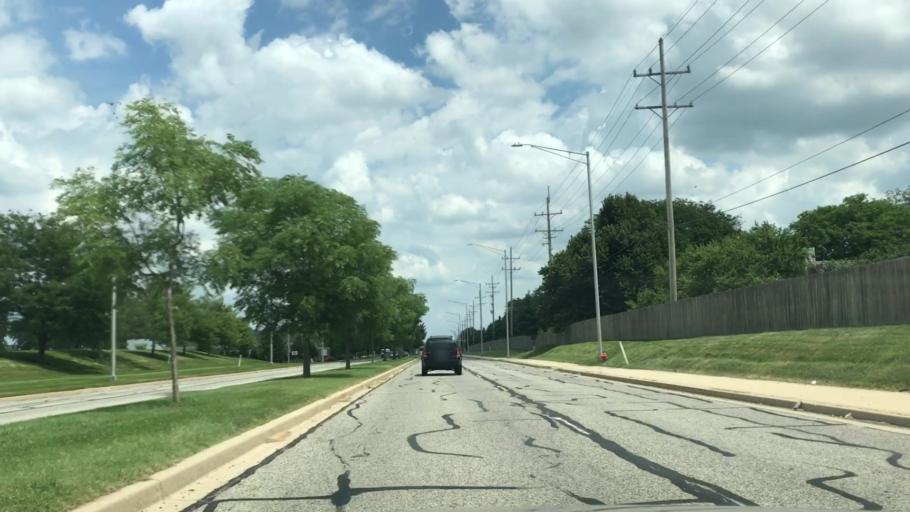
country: US
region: Illinois
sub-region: DuPage County
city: Warrenville
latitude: 41.7990
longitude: -88.2162
